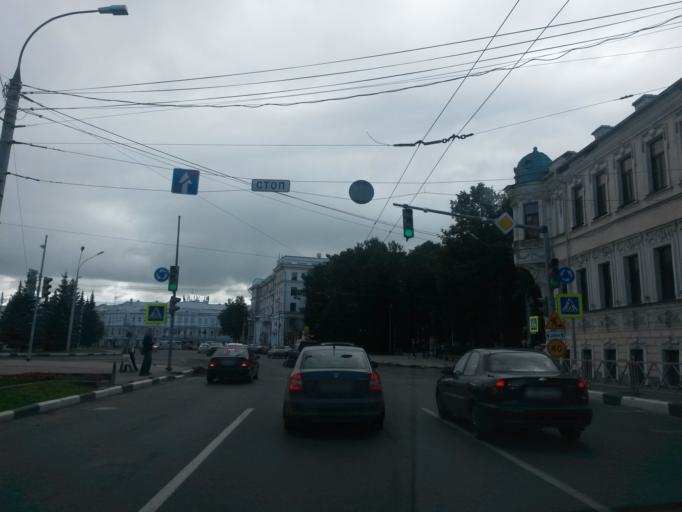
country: RU
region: Jaroslavl
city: Yaroslavl
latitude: 57.6271
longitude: 39.8841
